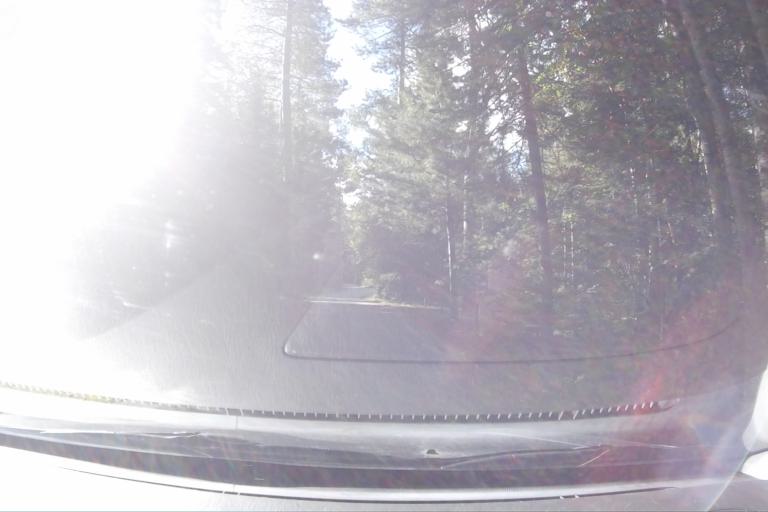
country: CA
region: Ontario
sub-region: Algoma
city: Sault Ste. Marie
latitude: 47.3277
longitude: -84.6115
